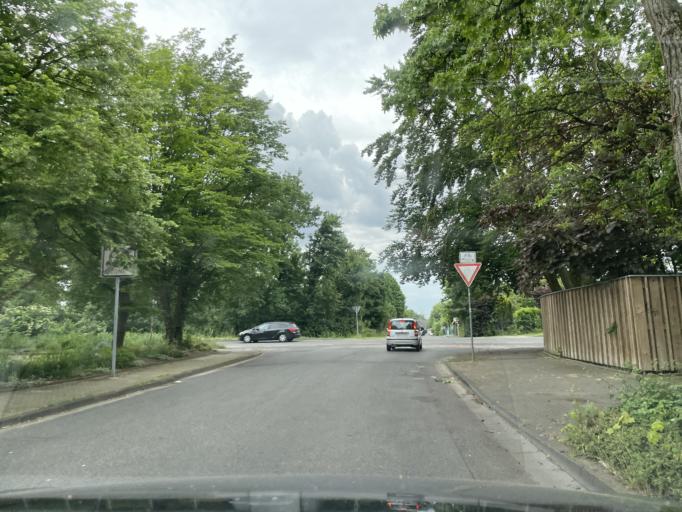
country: DE
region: North Rhine-Westphalia
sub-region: Regierungsbezirk Dusseldorf
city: Juchen
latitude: 51.1337
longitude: 6.4643
